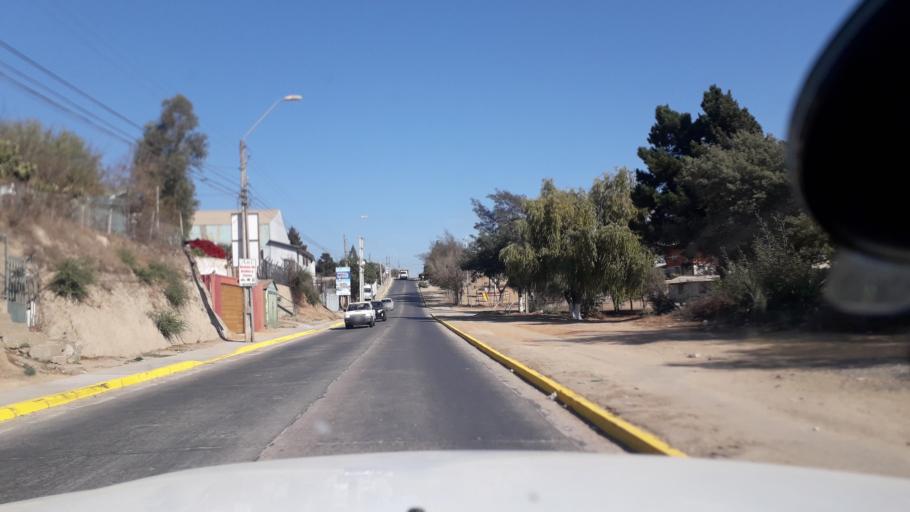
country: CL
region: Valparaiso
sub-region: Provincia de Marga Marga
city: Villa Alemana
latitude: -33.0623
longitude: -71.4026
